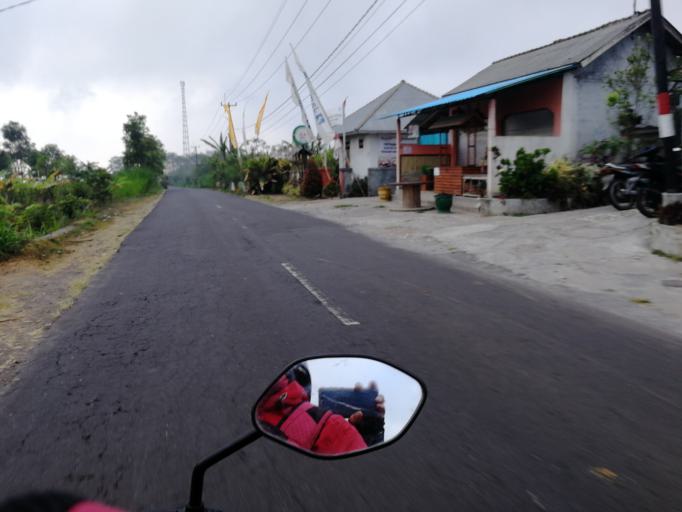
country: ID
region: Bali
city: Banjar Ambengan
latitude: -8.2390
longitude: 115.2415
